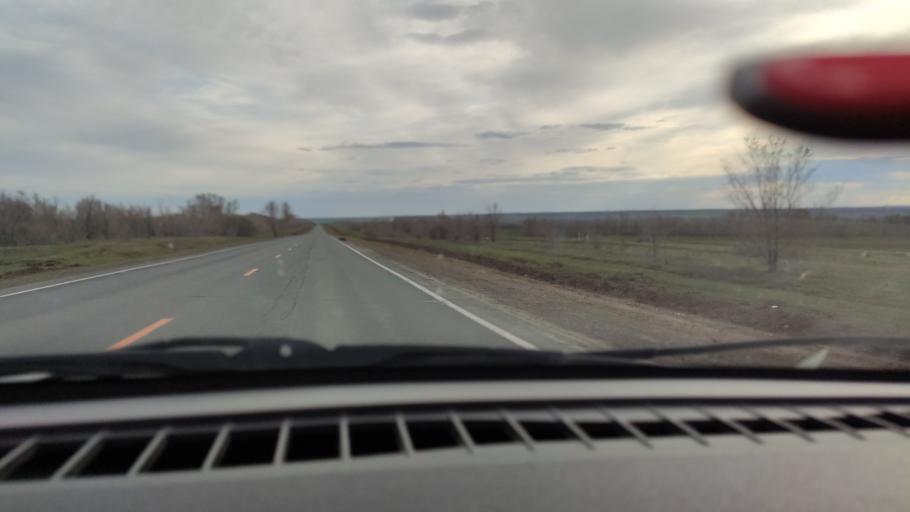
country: RU
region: Orenburg
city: Sakmara
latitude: 52.2444
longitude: 55.3523
